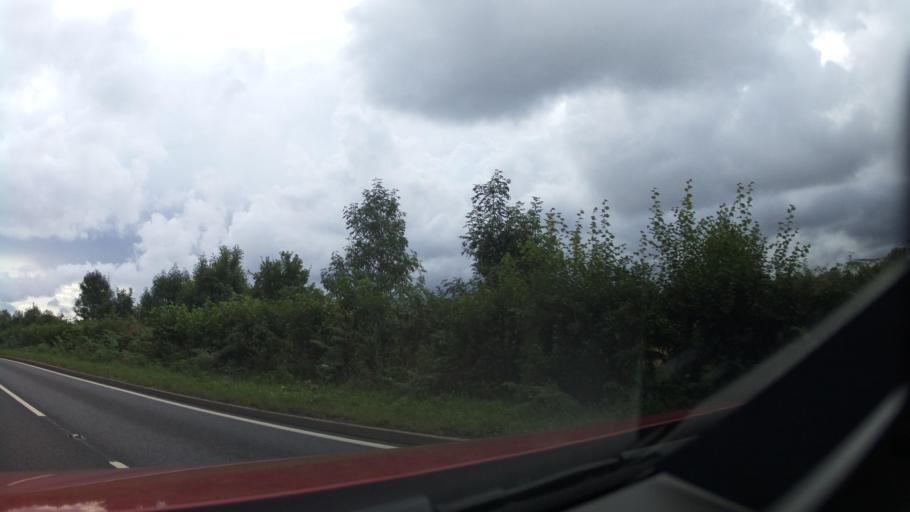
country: GB
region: England
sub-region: Shropshire
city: Bridgnorth
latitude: 52.5511
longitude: -2.4064
